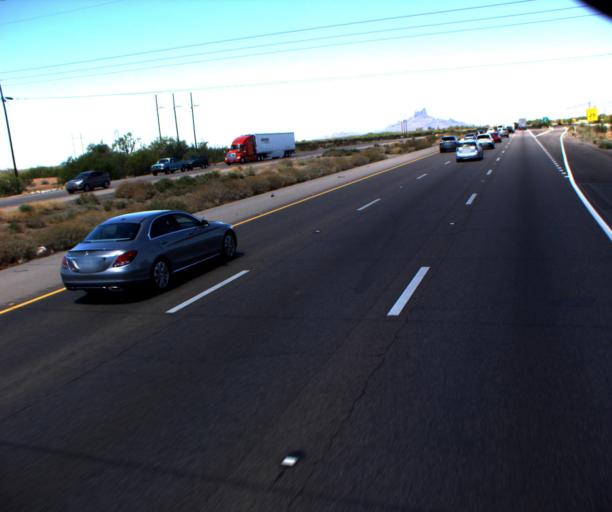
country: US
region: Arizona
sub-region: Pima County
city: Avra Valley
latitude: 32.5486
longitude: -111.3020
